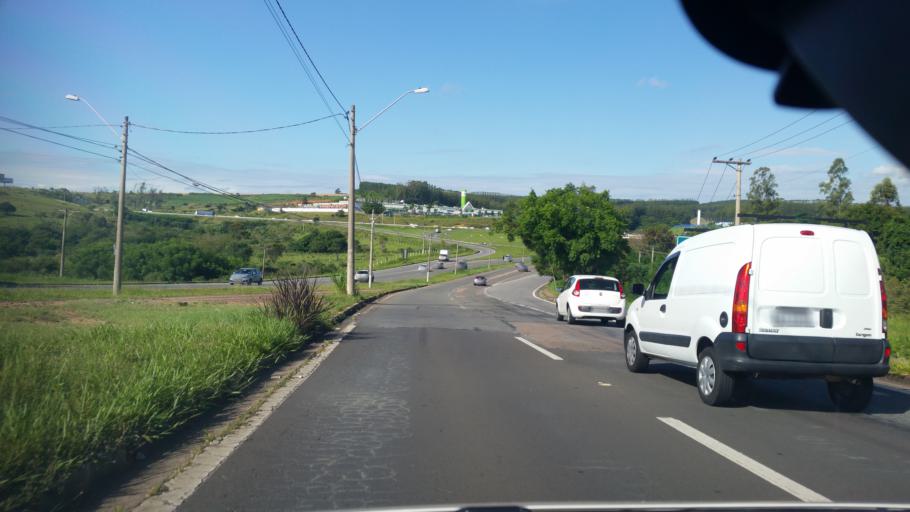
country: BR
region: Sao Paulo
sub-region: Campinas
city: Campinas
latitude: -22.8883
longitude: -47.0168
